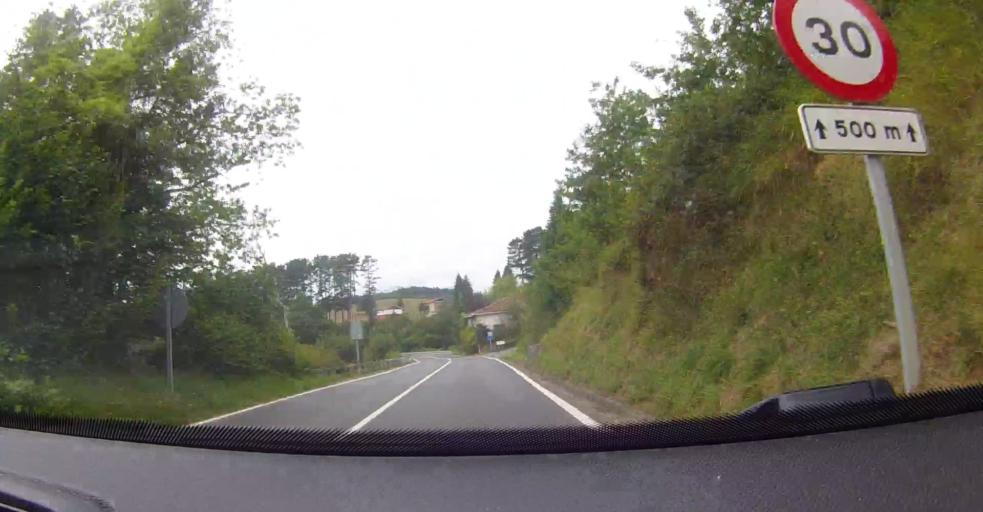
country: ES
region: Basque Country
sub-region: Bizkaia
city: Lanestosa
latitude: 43.2407
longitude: -3.3225
